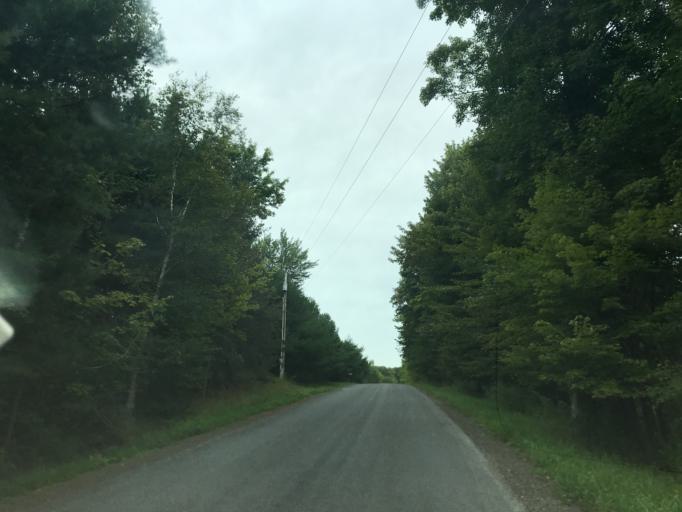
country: US
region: New York
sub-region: Otsego County
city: Worcester
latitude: 42.5229
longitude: -74.6635
